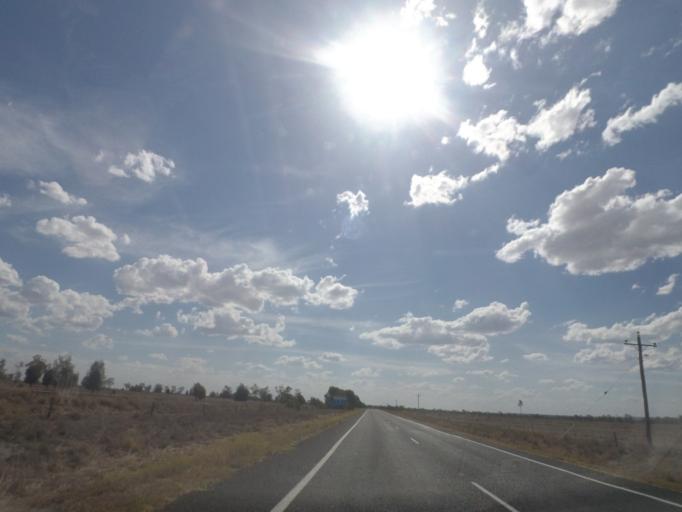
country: AU
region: New South Wales
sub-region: Moree Plains
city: Boggabilla
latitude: -28.4148
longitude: 151.1349
